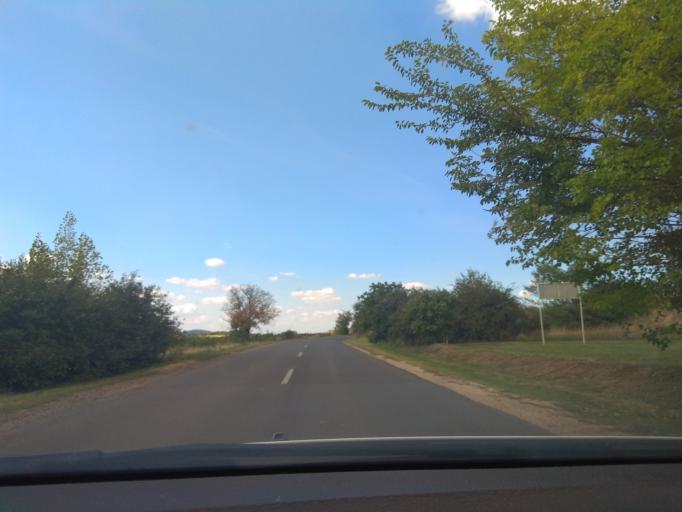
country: HU
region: Borsod-Abauj-Zemplen
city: Mad
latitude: 48.1959
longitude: 21.2622
